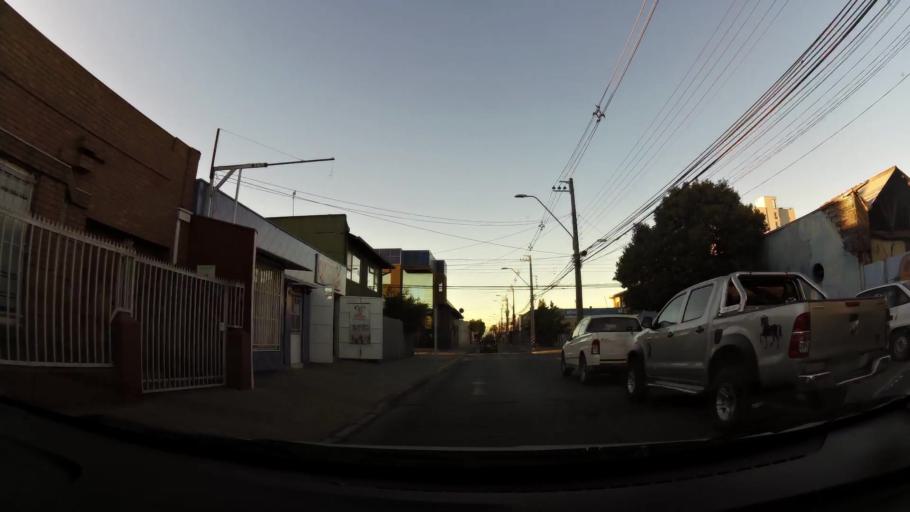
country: CL
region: Maule
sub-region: Provincia de Curico
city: Curico
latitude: -34.9881
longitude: -71.2355
